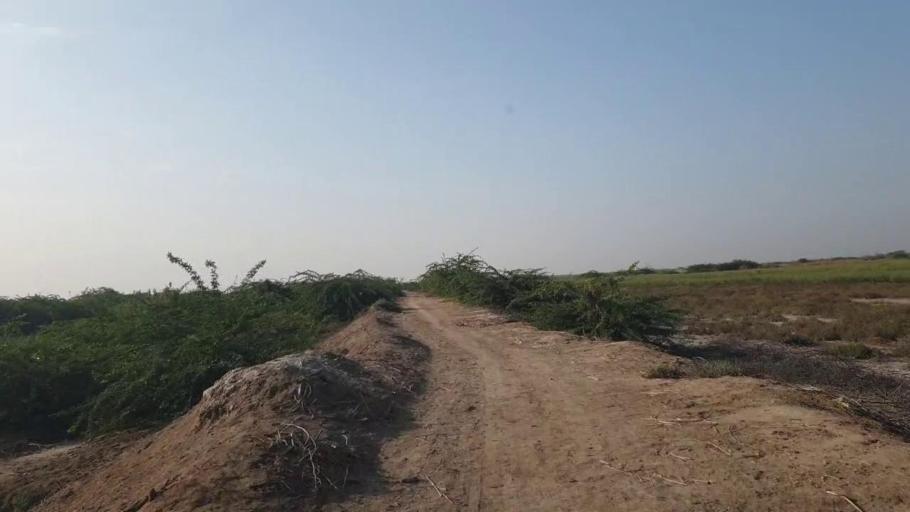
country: PK
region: Sindh
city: Badin
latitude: 24.4524
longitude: 68.7330
